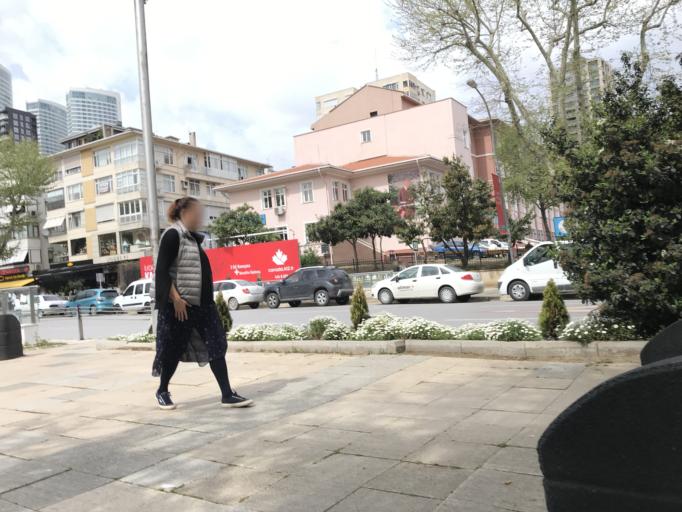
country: TR
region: Istanbul
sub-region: Atasehir
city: Atasehir
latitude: 40.9724
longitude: 29.0577
